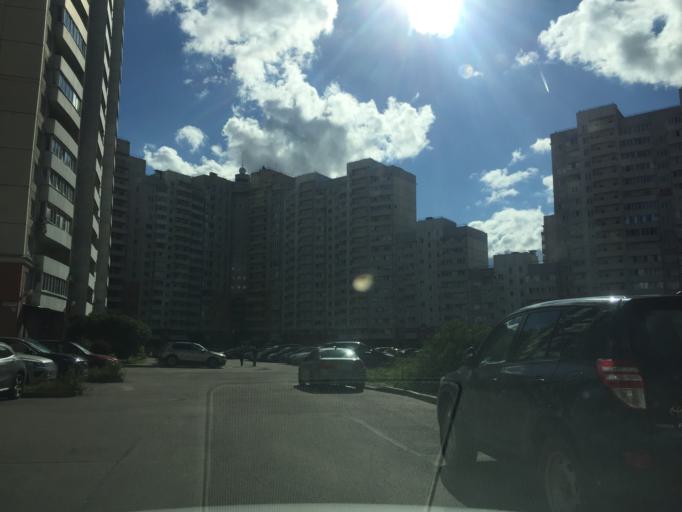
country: RU
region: St.-Petersburg
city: Kupchino
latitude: 59.8276
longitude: 30.3294
